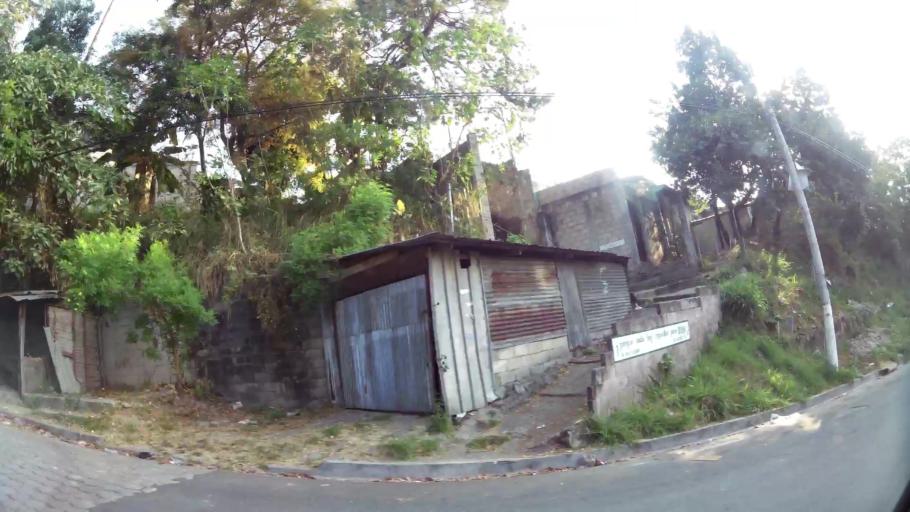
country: SV
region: San Salvador
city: San Salvador
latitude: 13.6786
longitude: -89.2038
